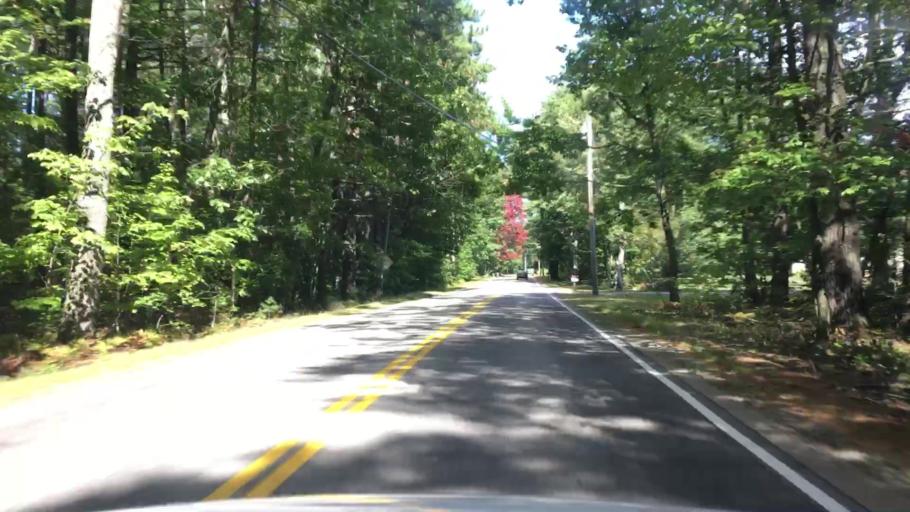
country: US
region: Maine
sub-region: Cumberland County
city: West Scarborough
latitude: 43.5951
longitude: -70.4302
